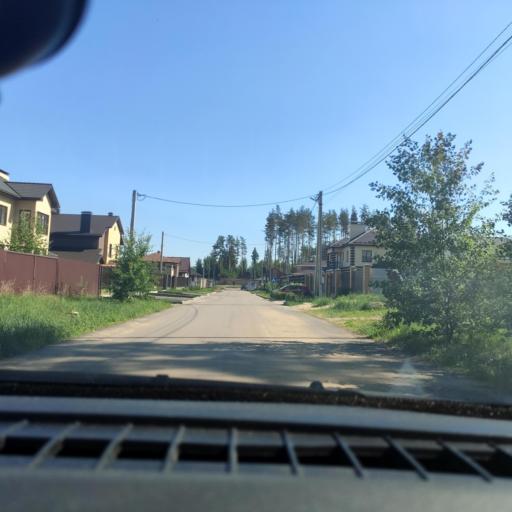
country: RU
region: Voronezj
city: Podgornoye
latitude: 51.7817
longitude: 39.1476
